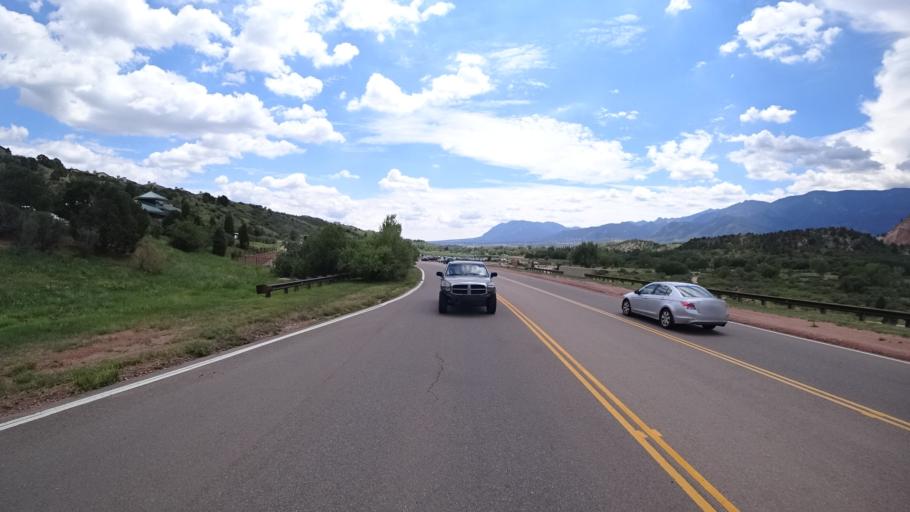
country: US
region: Colorado
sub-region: El Paso County
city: Manitou Springs
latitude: 38.8792
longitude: -104.8710
